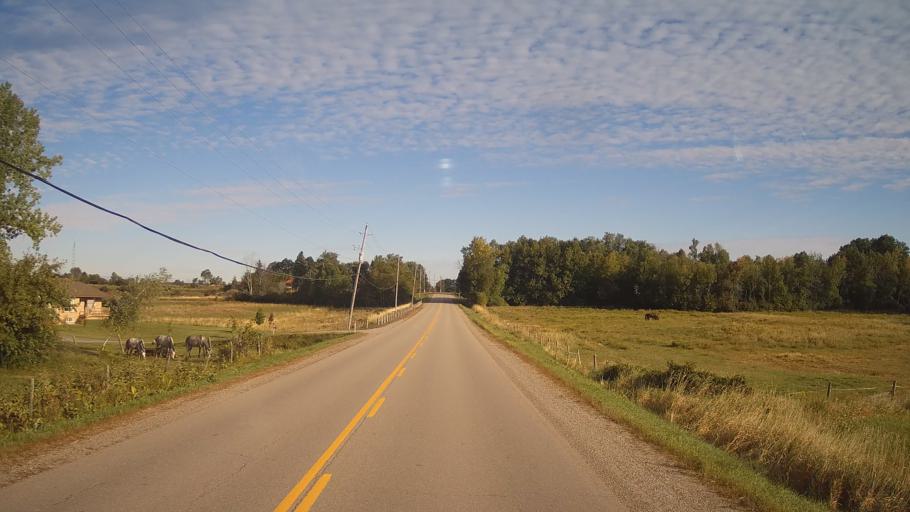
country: CA
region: Ontario
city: Gananoque
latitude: 44.3628
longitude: -76.1357
